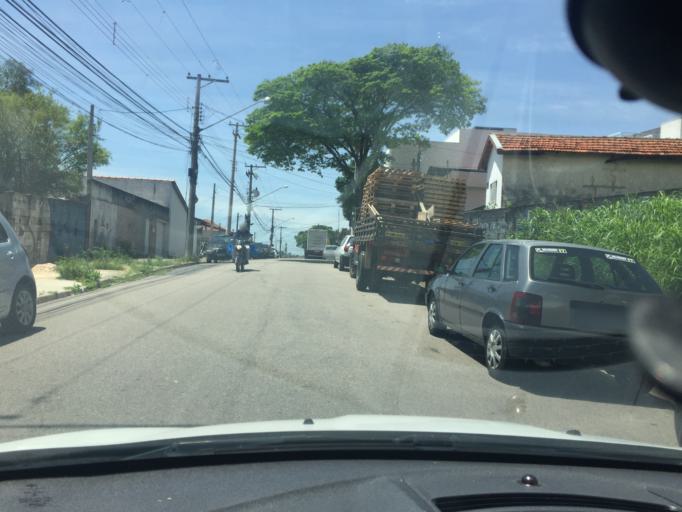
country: BR
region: Sao Paulo
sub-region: Jundiai
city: Jundiai
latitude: -23.2272
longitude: -46.8807
